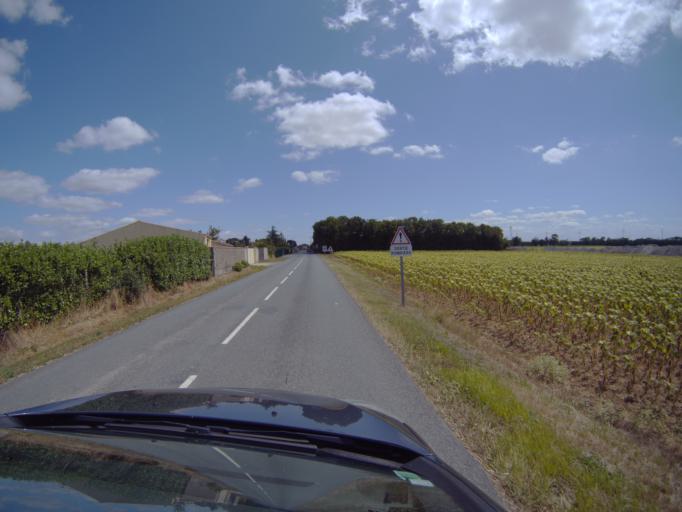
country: FR
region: Poitou-Charentes
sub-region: Departement de la Charente-Maritime
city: Saint-Jean-de-Liversay
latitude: 46.2664
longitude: -0.8773
